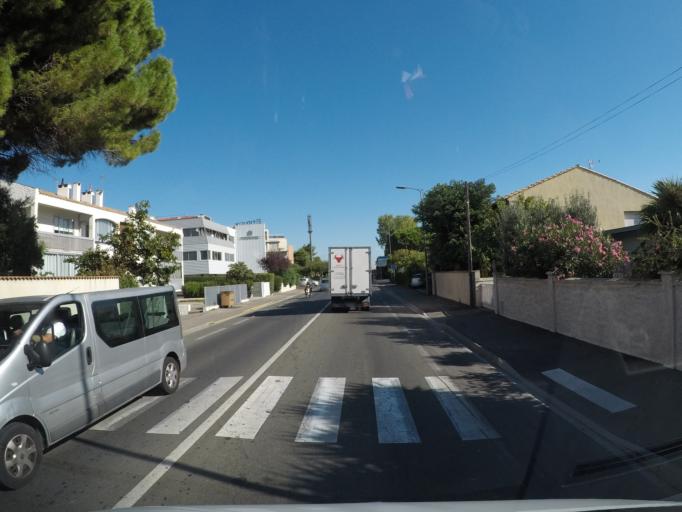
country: FR
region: Languedoc-Roussillon
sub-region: Departement de l'Aude
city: Narbonne
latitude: 43.1788
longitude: 3.0127
